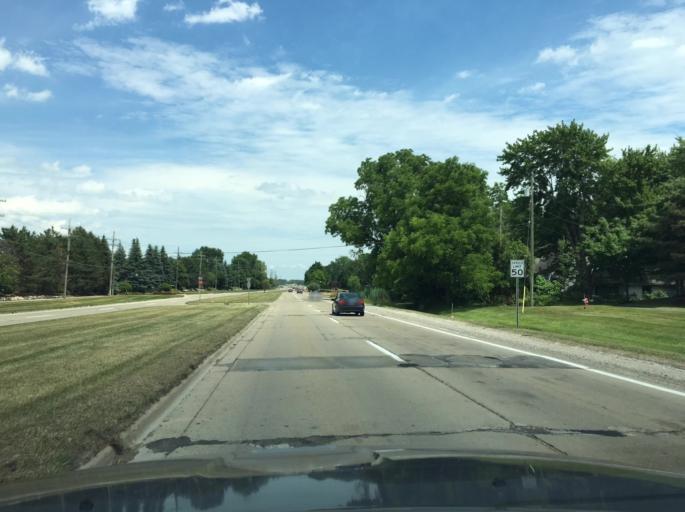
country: US
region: Michigan
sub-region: Macomb County
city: Shelby
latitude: 42.7136
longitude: -83.0453
